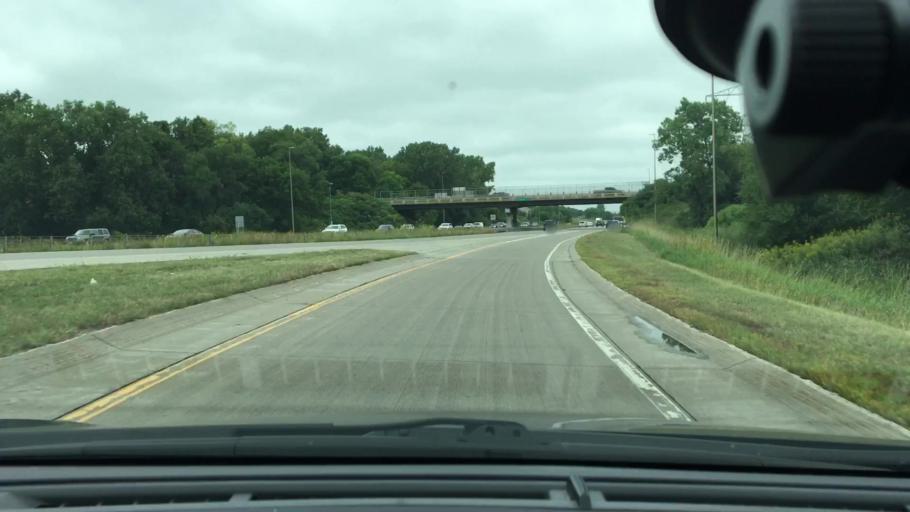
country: US
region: Minnesota
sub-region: Hennepin County
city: Plymouth
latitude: 44.9740
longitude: -93.4600
